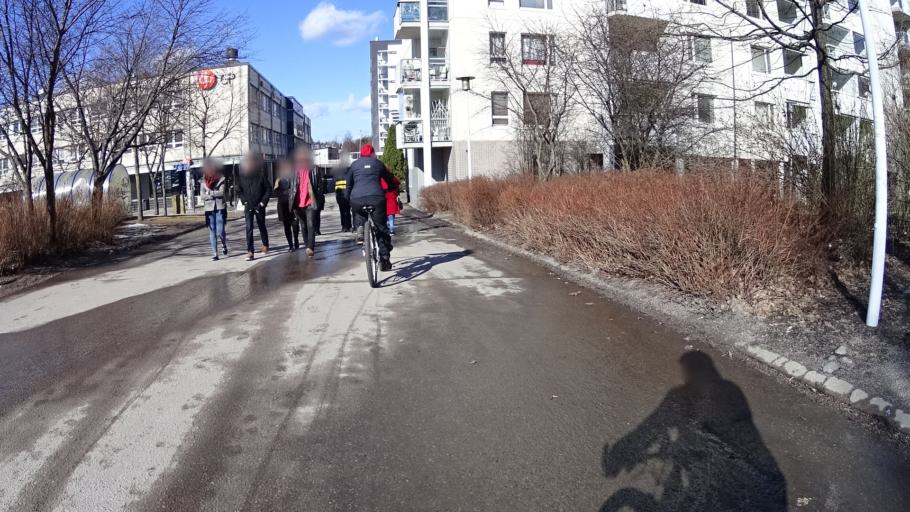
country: FI
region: Uusimaa
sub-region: Helsinki
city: Teekkarikylae
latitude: 60.2623
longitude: 24.8525
